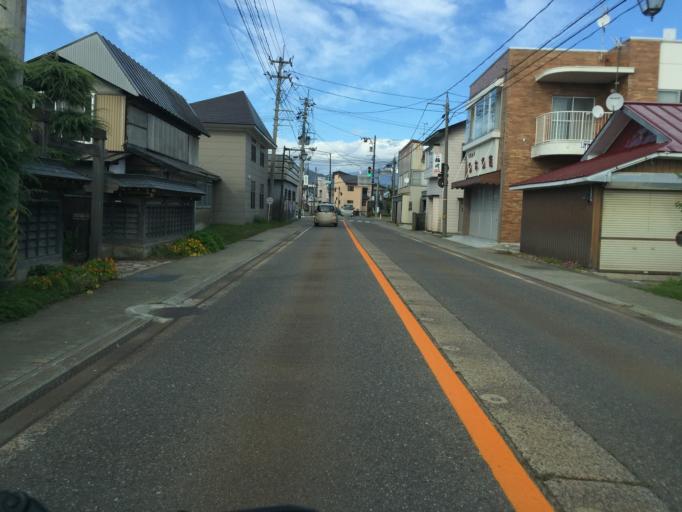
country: JP
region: Fukushima
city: Inawashiro
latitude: 37.5562
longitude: 140.1062
